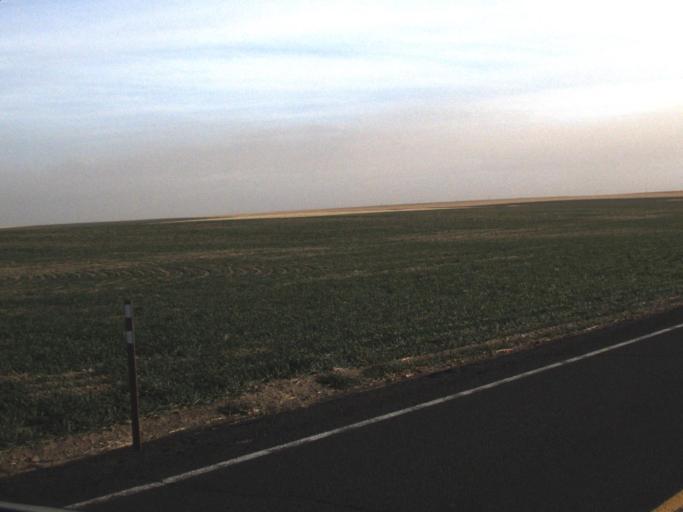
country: US
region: Washington
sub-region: Adams County
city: Ritzville
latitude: 47.2792
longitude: -118.6907
